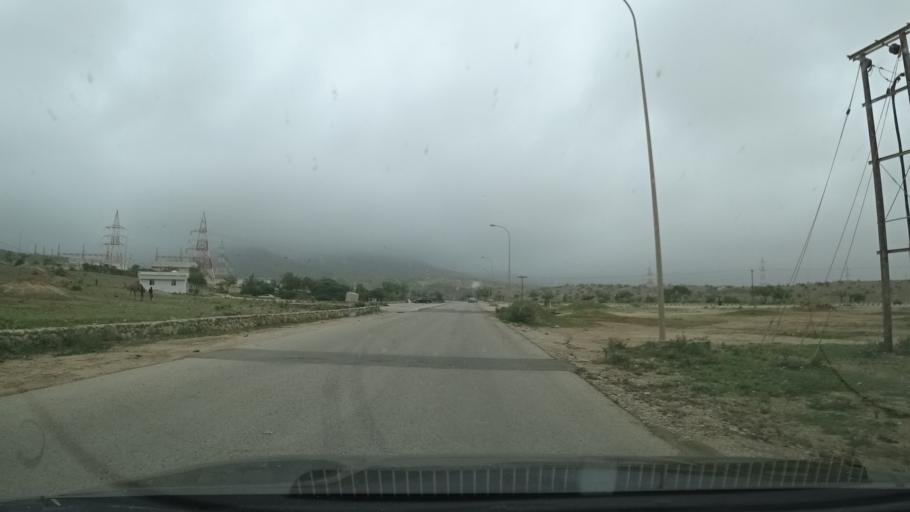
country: OM
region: Zufar
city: Salalah
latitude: 17.0890
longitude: 54.0782
